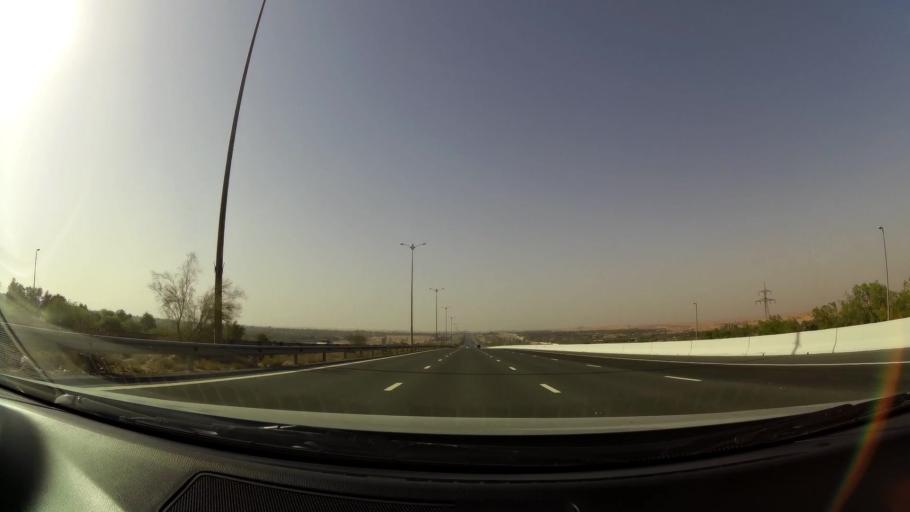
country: OM
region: Al Buraimi
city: Al Buraymi
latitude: 24.5744
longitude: 55.7461
